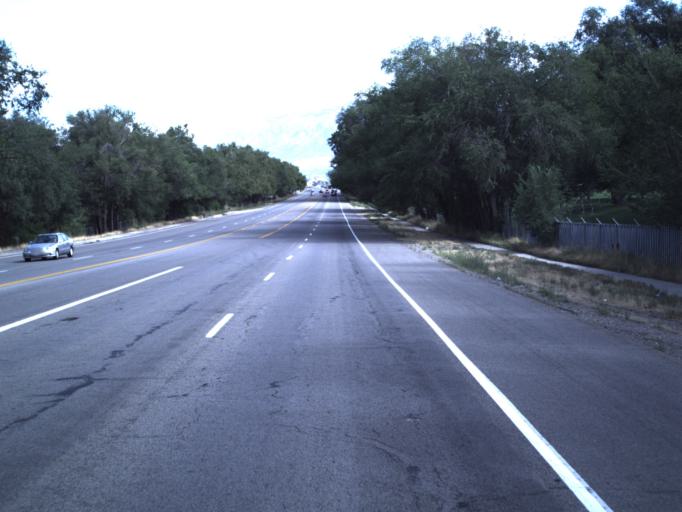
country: US
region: Utah
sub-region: Weber County
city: South Ogden
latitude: 41.1850
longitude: -111.9712
